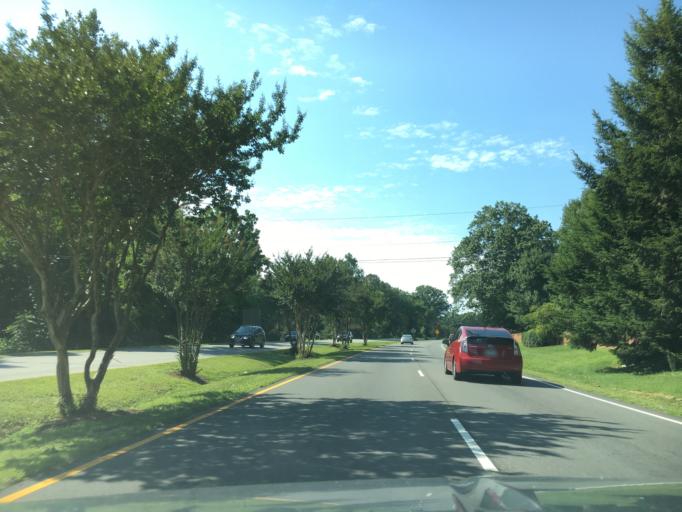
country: US
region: Virginia
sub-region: Halifax County
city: South Boston
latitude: 36.7181
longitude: -78.9168
